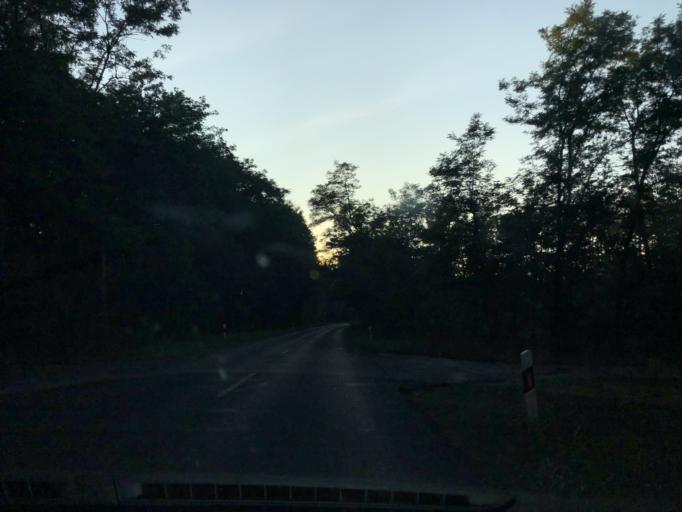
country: DE
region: Brandenburg
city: Mullrose
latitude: 52.2487
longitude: 14.4475
